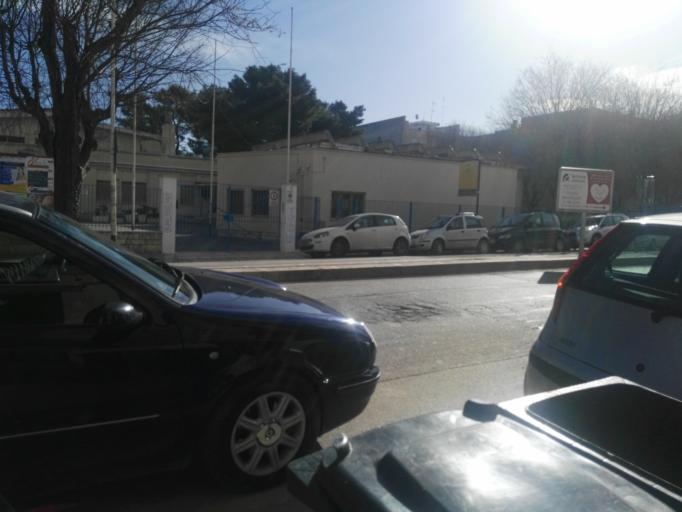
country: IT
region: Apulia
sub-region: Provincia di Barletta - Andria - Trani
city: Andria
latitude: 41.2249
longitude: 16.3069
